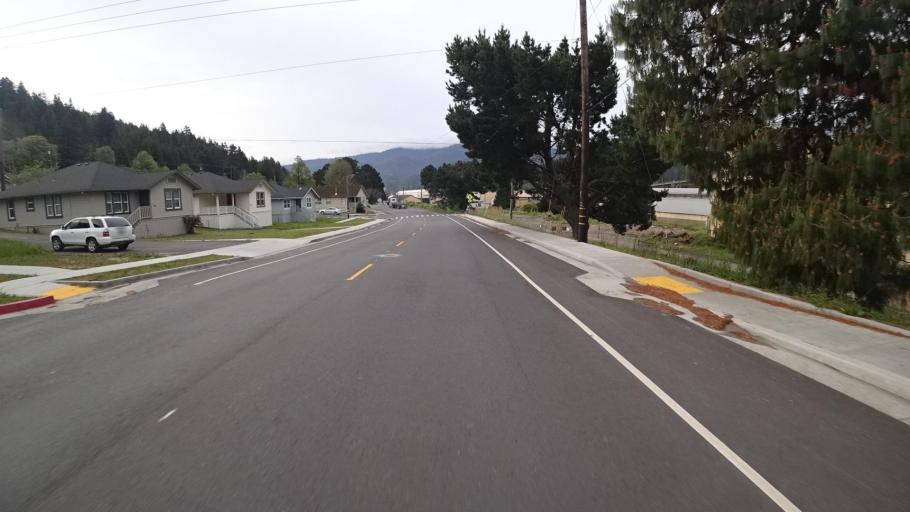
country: US
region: California
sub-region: Humboldt County
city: Rio Dell
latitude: 40.4790
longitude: -124.1029
